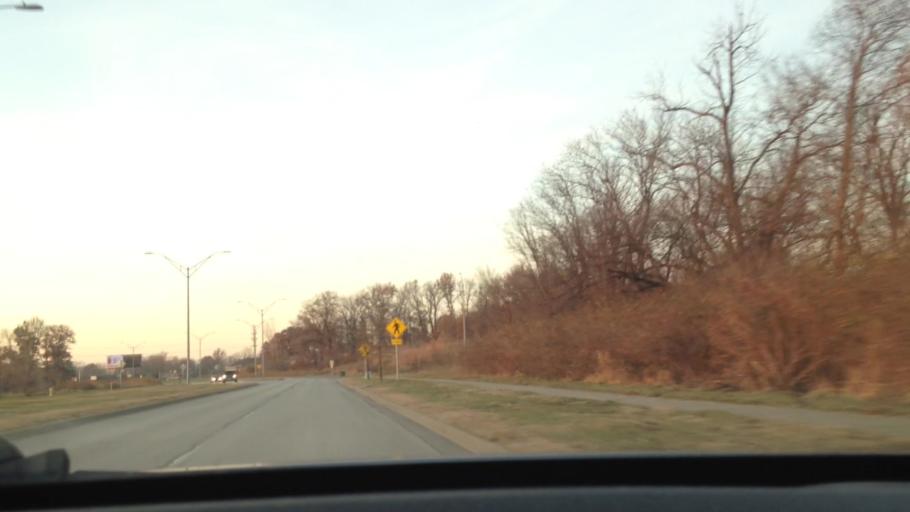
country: US
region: Missouri
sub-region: Clay County
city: Pleasant Valley
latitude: 39.2139
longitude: -94.4703
